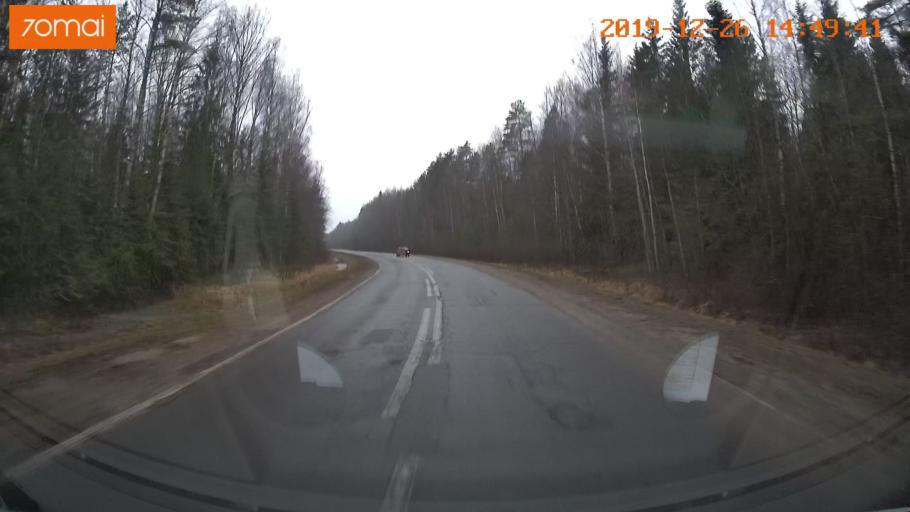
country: RU
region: Jaroslavl
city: Poshekhon'ye
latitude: 58.3379
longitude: 38.9397
